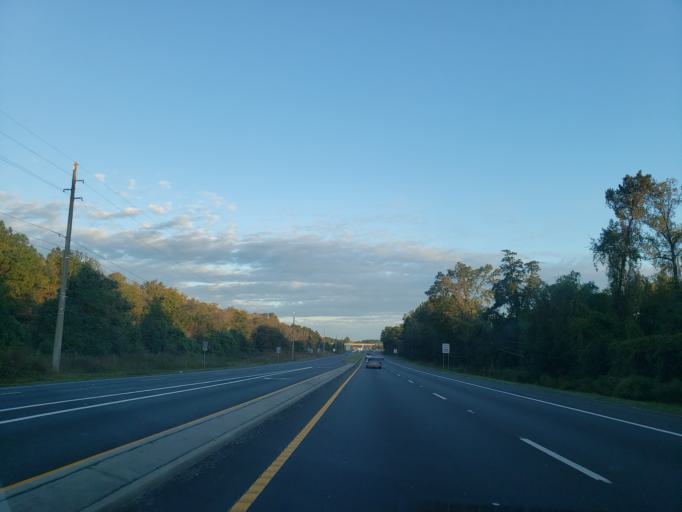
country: US
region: Georgia
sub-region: Chatham County
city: Port Wentworth
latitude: 32.1551
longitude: -81.1812
